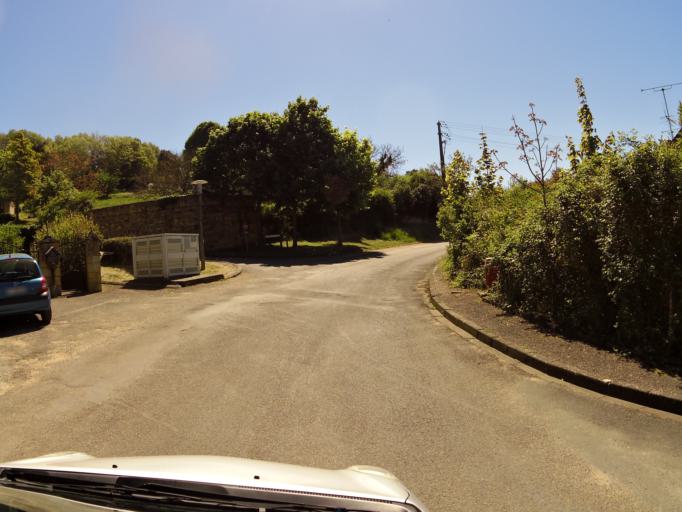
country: FR
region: Aquitaine
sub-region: Departement de la Dordogne
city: Domme
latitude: 44.8004
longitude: 1.2209
